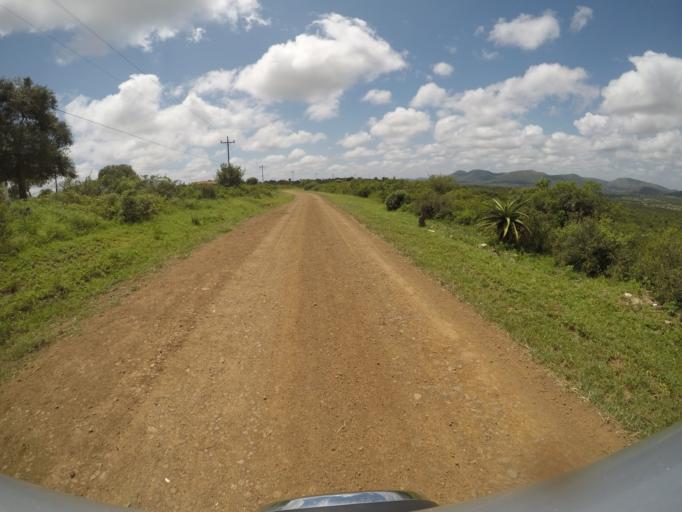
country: ZA
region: KwaZulu-Natal
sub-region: uThungulu District Municipality
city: Empangeni
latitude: -28.5876
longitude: 31.8213
